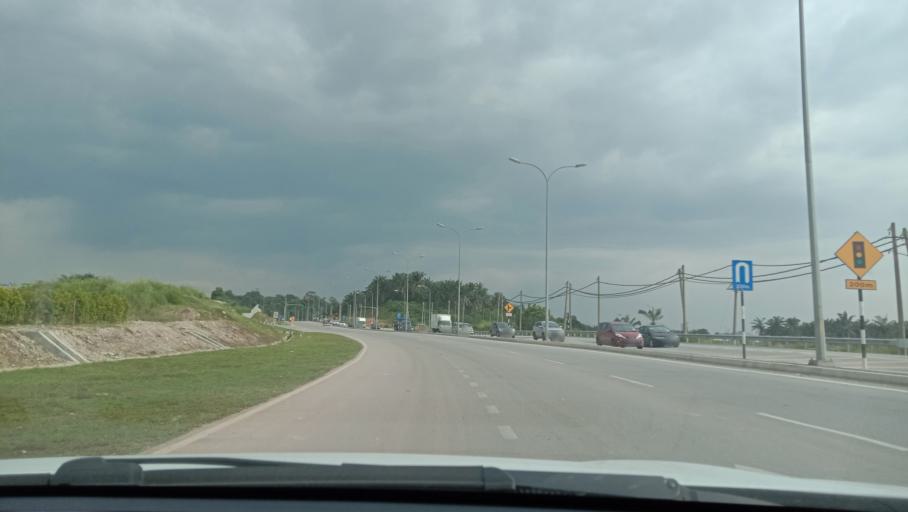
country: MY
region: Selangor
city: Ladang Seri Kundang
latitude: 3.2413
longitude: 101.4753
